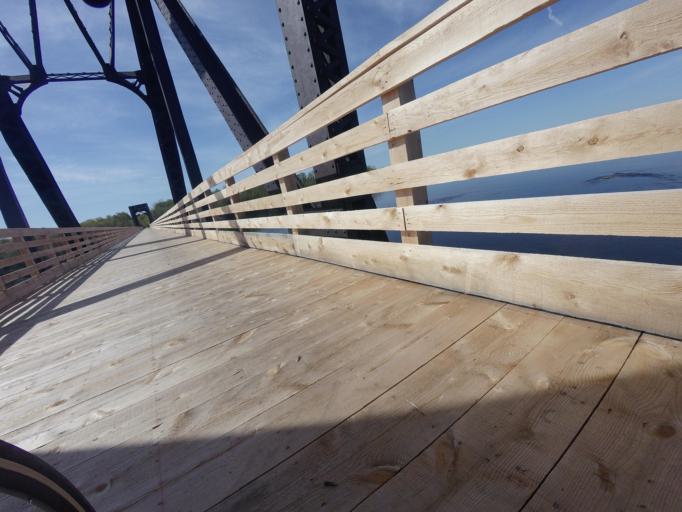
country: CA
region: Ontario
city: Arnprior
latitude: 45.4664
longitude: -76.2862
